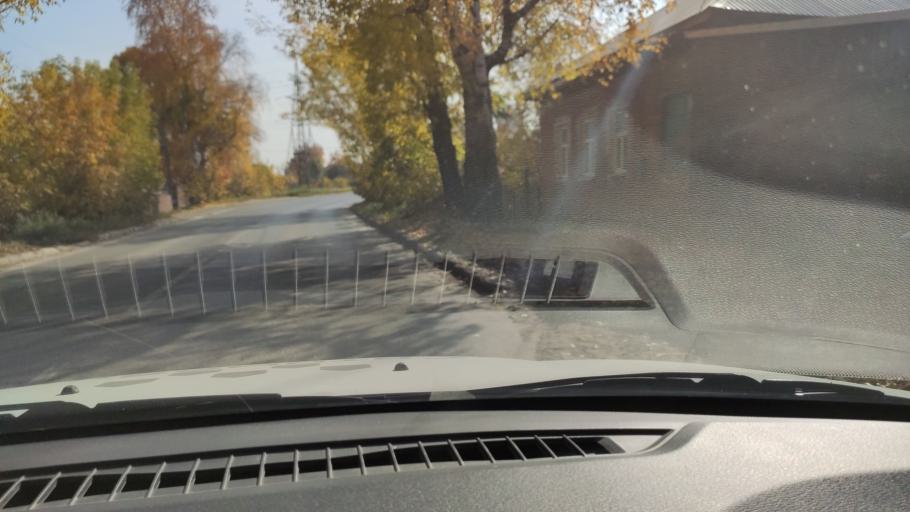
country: RU
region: Perm
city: Perm
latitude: 58.0111
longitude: 56.3203
